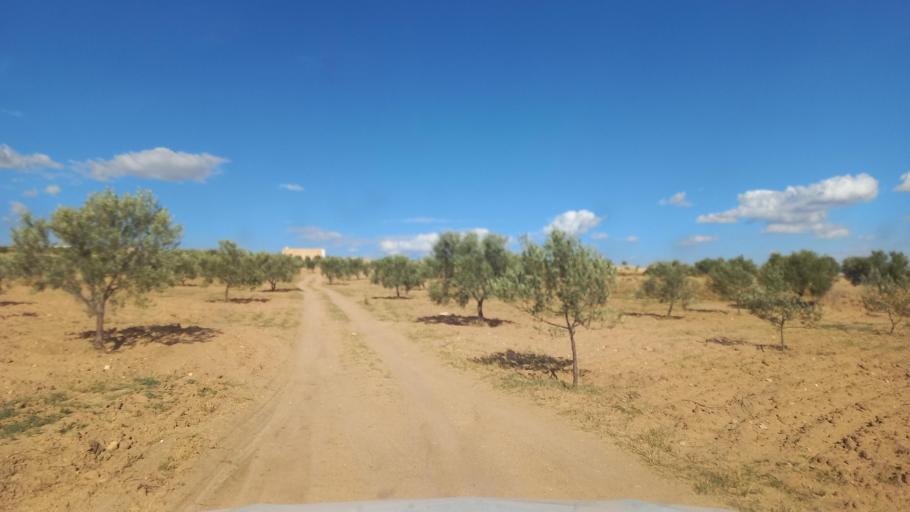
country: TN
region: Al Qasrayn
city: Sbiba
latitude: 35.4005
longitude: 9.0116
